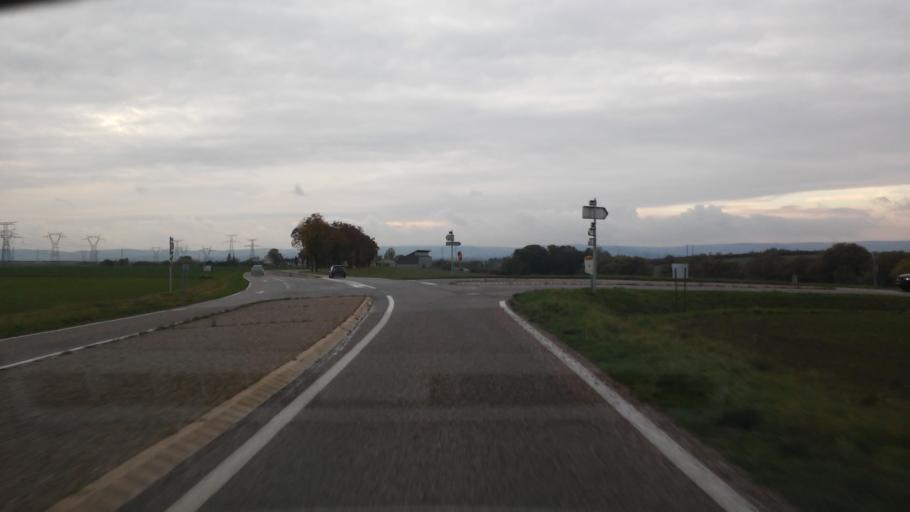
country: FR
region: Lorraine
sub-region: Departement de la Moselle
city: Vigy
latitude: 49.1980
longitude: 6.2609
